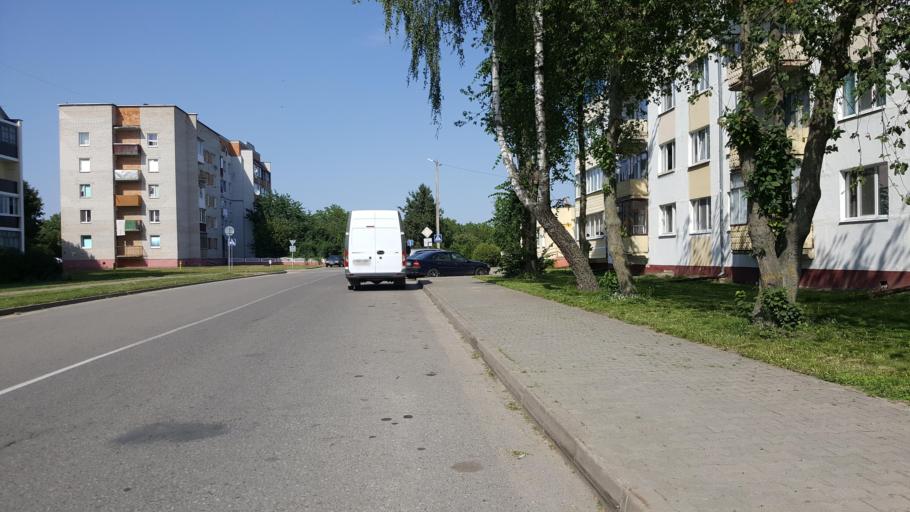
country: BY
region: Brest
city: Zhabinka
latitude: 52.1955
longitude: 24.0204
